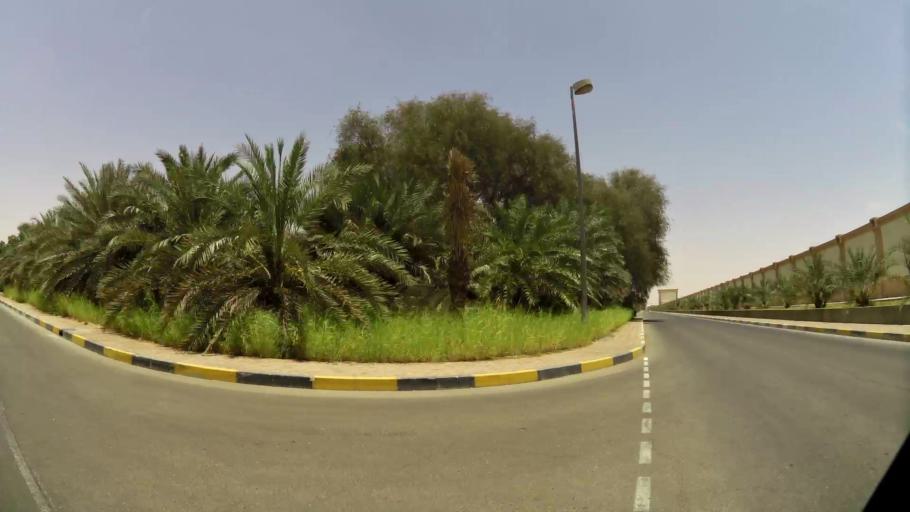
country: OM
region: Al Buraimi
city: Al Buraymi
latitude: 24.2757
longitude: 55.7367
